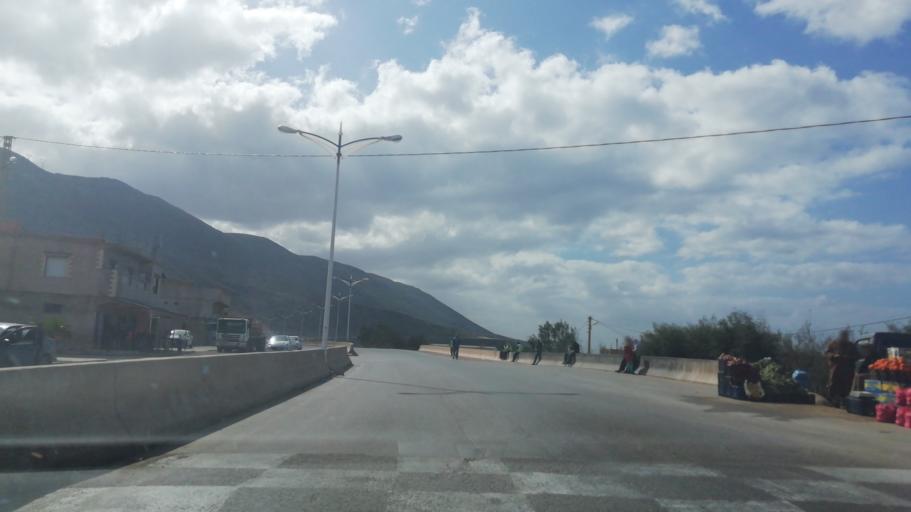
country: DZ
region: Mostaganem
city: Mostaganem
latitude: 36.0216
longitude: 0.1318
